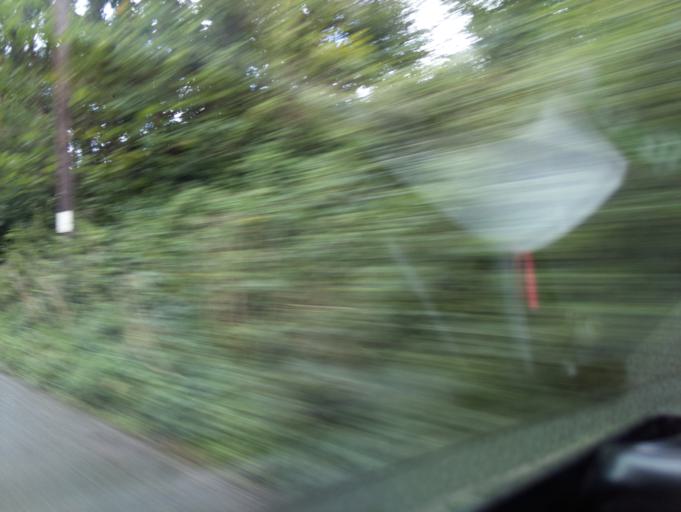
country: GB
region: England
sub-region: Devon
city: Modbury
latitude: 50.3371
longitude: -3.8560
